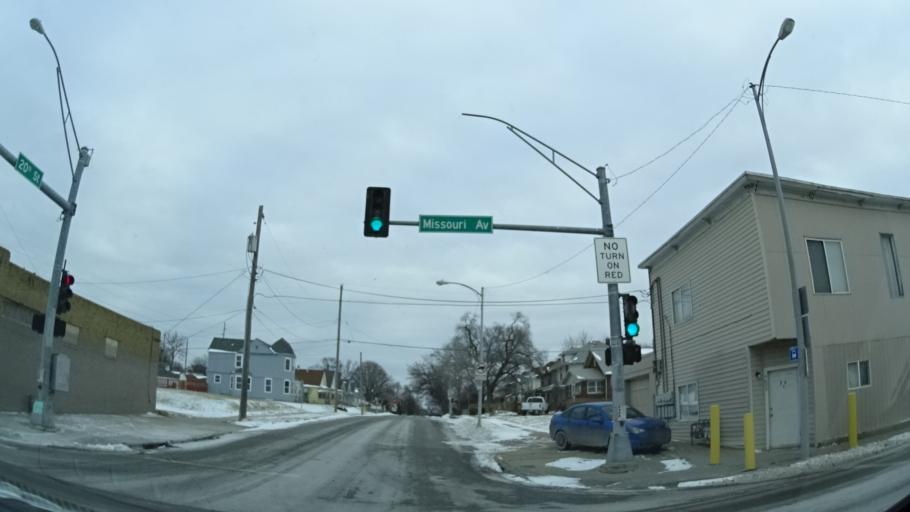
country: US
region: Nebraska
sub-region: Douglas County
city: Omaha
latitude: 41.2129
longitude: -95.9417
